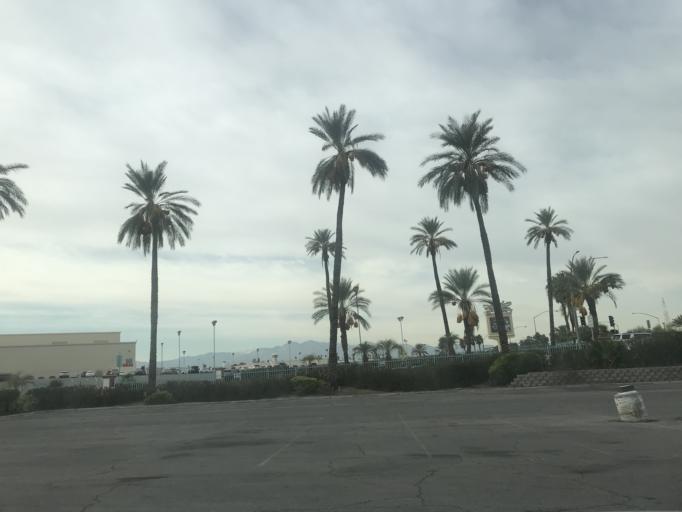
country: US
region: Nevada
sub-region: Clark County
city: Paradise
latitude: 36.1206
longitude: -115.1839
